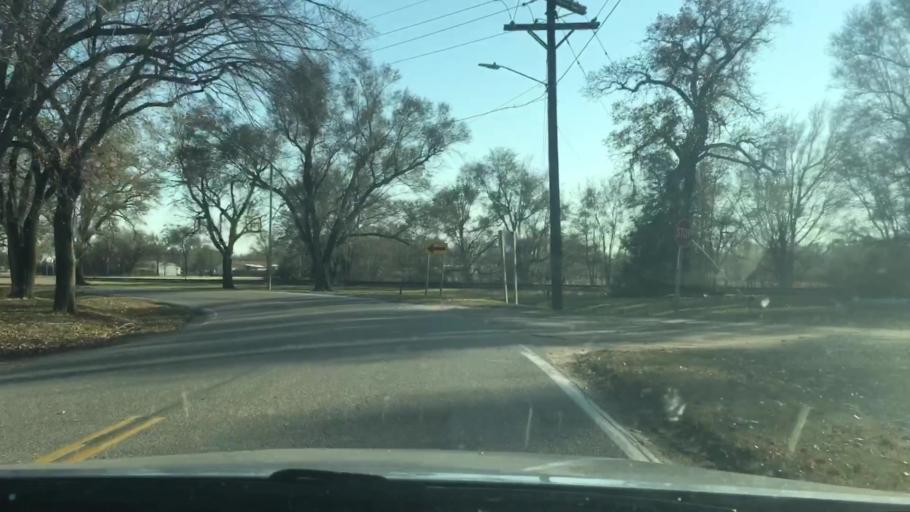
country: US
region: Kansas
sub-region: Reno County
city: Nickerson
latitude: 38.1501
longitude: -98.0873
